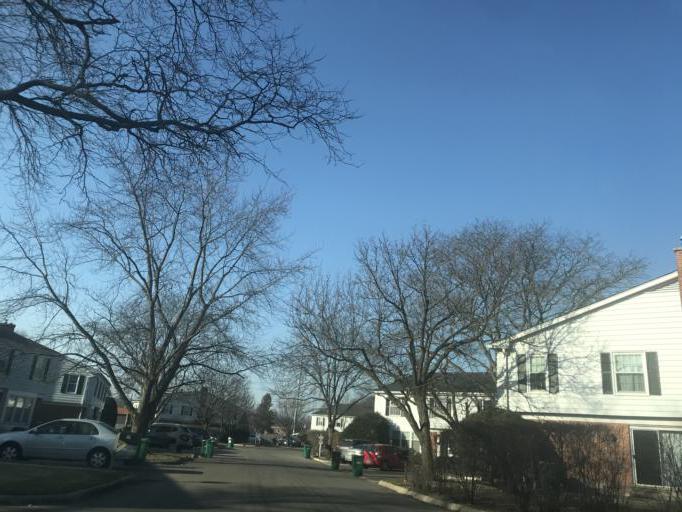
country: US
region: Illinois
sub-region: Cook County
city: Northfield
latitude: 42.0965
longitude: -87.7666
